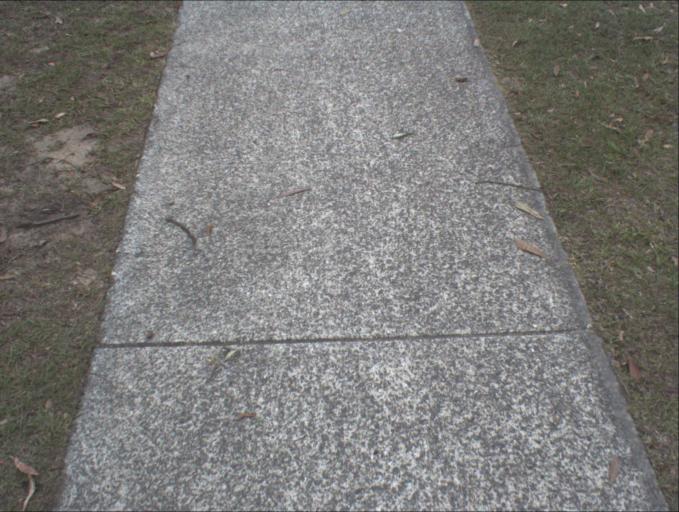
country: AU
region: Queensland
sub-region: Logan
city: Logan Reserve
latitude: -27.6828
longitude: 153.0833
